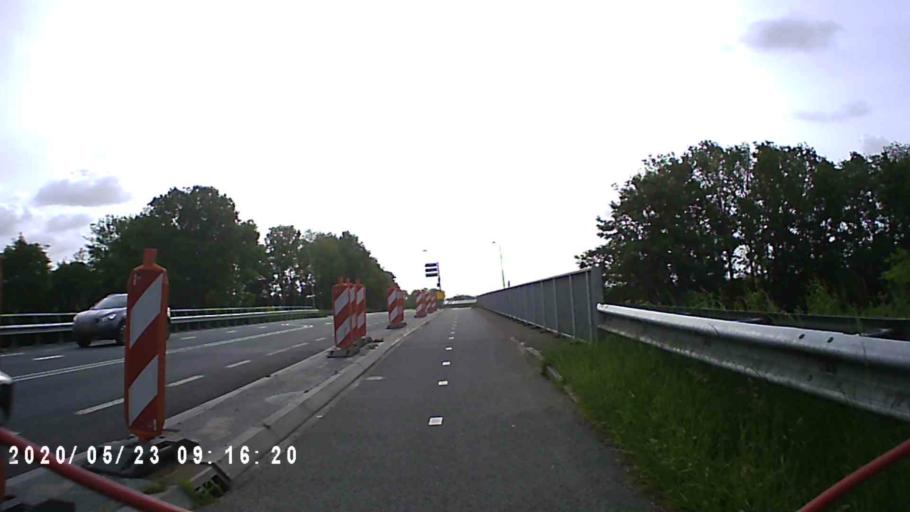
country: NL
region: Groningen
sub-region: Gemeente Bedum
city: Bedum
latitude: 53.3019
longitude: 6.6502
